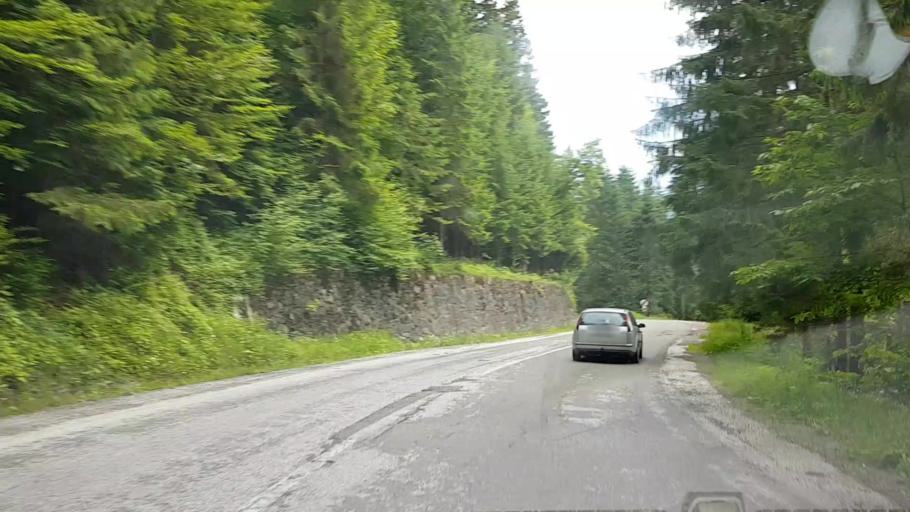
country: RO
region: Neamt
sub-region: Comuna Pangarati
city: Pangarati
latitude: 46.9702
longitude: 26.1177
